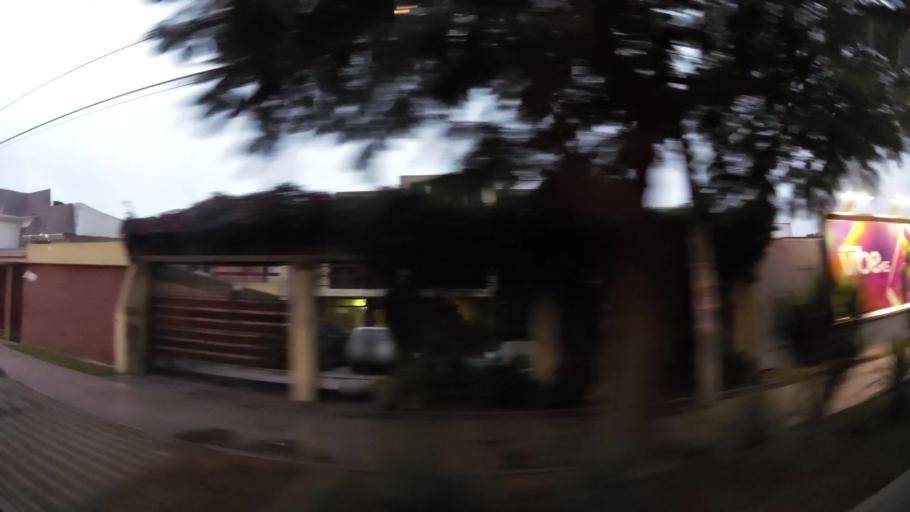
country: PE
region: Lima
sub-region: Lima
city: La Molina
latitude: -12.0971
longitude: -76.9513
